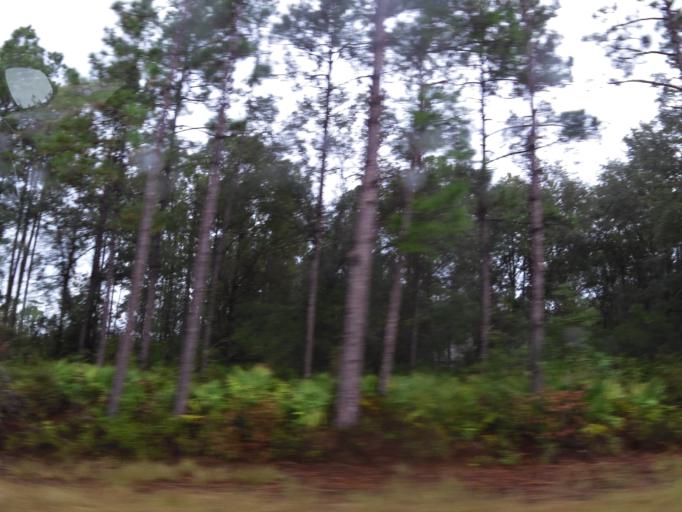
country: US
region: Georgia
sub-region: Wayne County
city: Jesup
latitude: 31.5767
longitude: -81.8485
